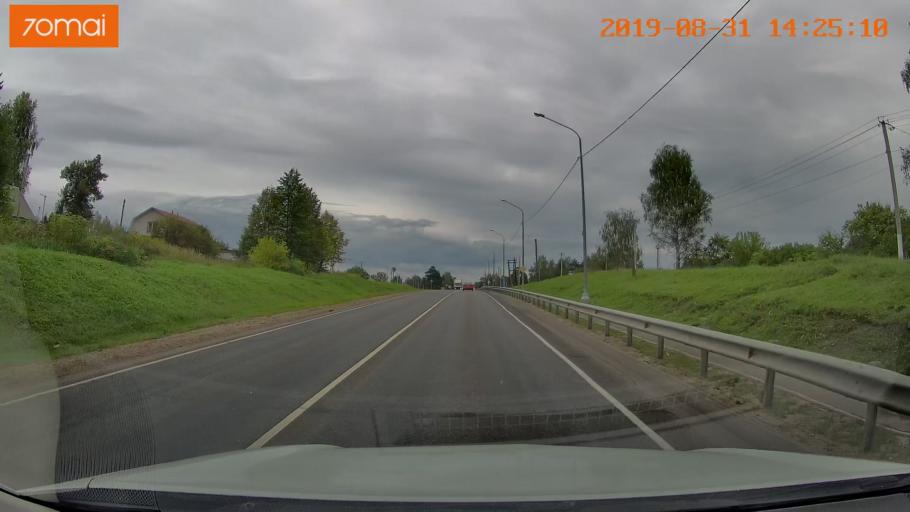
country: RU
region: Smolensk
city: Yekimovichi
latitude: 54.1070
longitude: 33.2687
